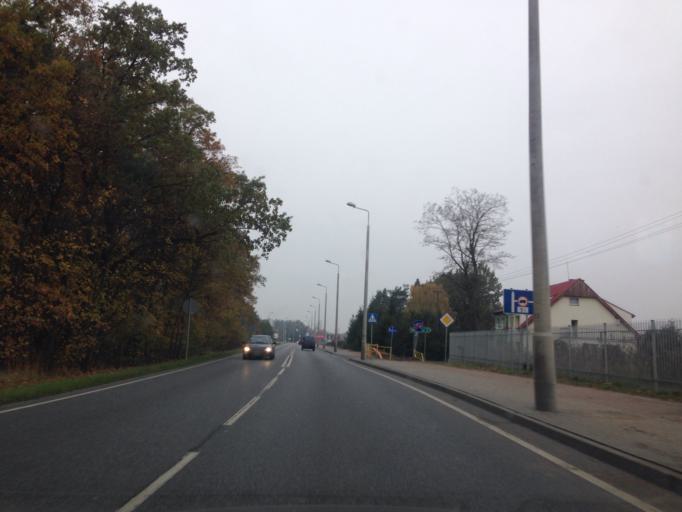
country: PL
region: Kujawsko-Pomorskie
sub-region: Grudziadz
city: Grudziadz
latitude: 53.4532
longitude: 18.7957
